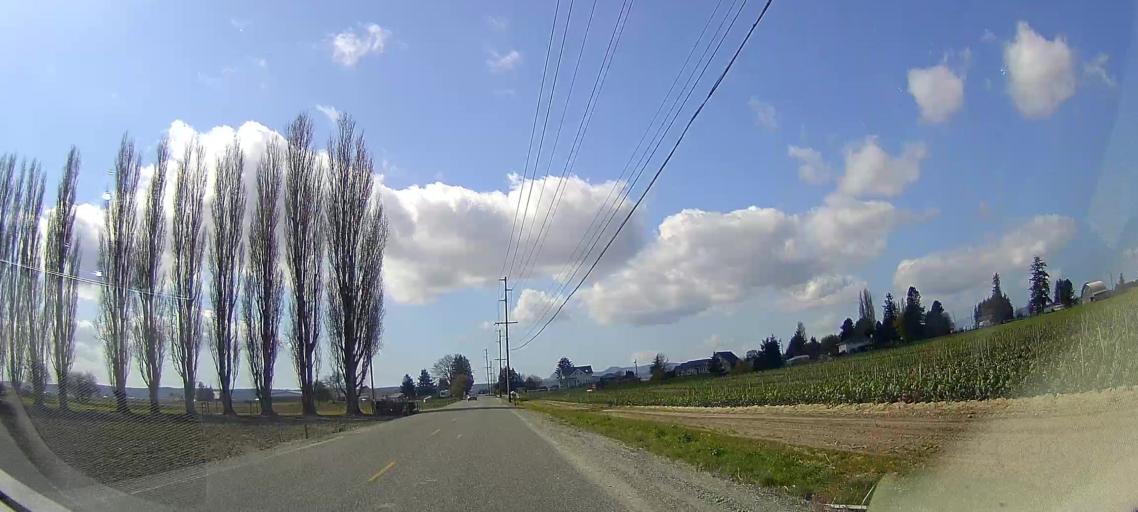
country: US
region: Washington
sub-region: Skagit County
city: Mount Vernon
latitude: 48.4427
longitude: -122.4358
